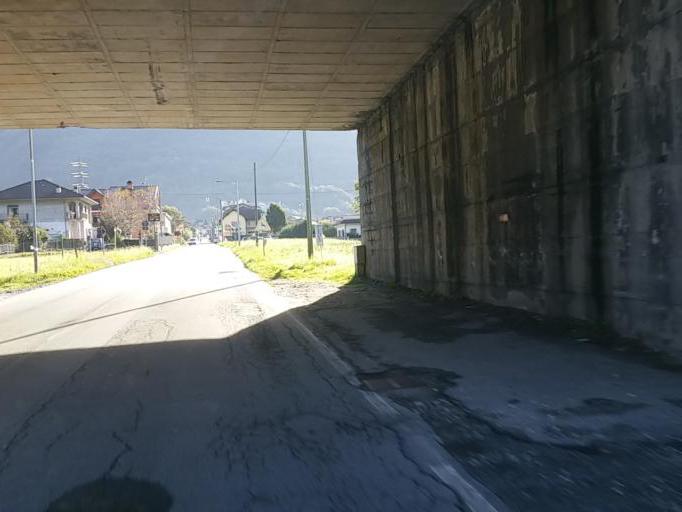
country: IT
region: Piedmont
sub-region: Provincia Verbano-Cusio-Ossola
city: Crevoladossola
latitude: 46.1508
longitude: 8.3119
